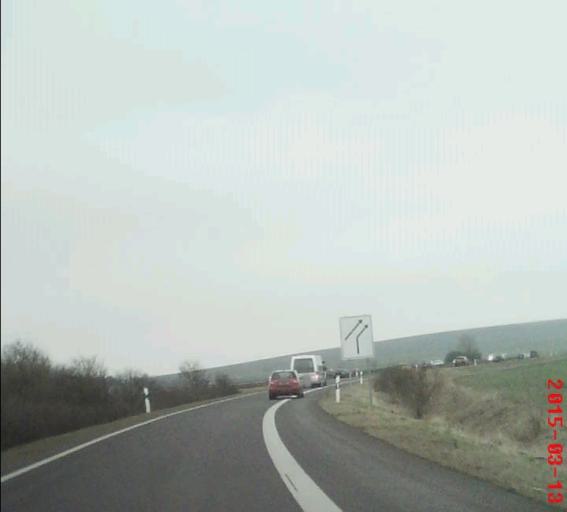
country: DE
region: Thuringia
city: Andisleben
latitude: 51.0808
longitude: 10.9203
